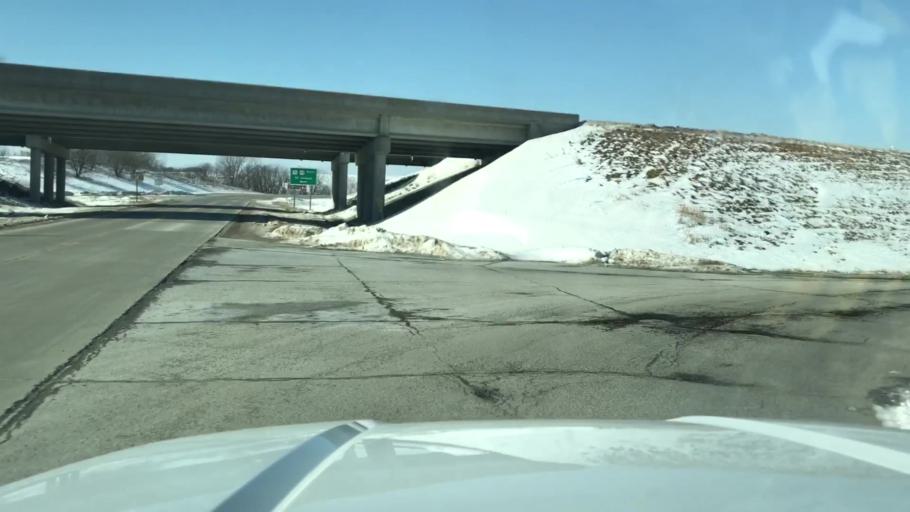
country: US
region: Missouri
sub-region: Andrew County
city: Savannah
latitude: 39.9618
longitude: -94.8607
